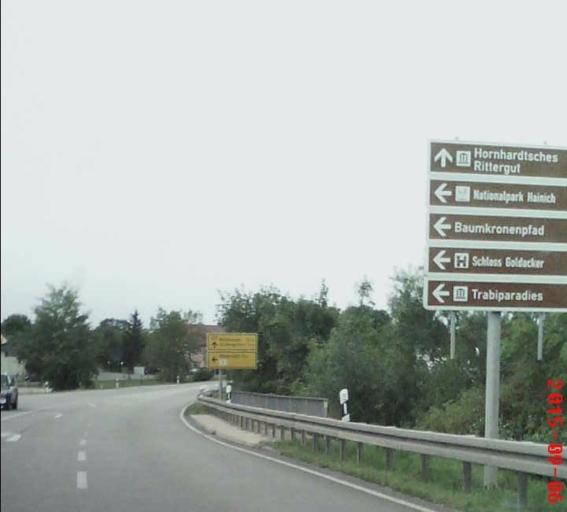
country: DE
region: Thuringia
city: Schonstedt
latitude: 51.1226
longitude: 10.5881
